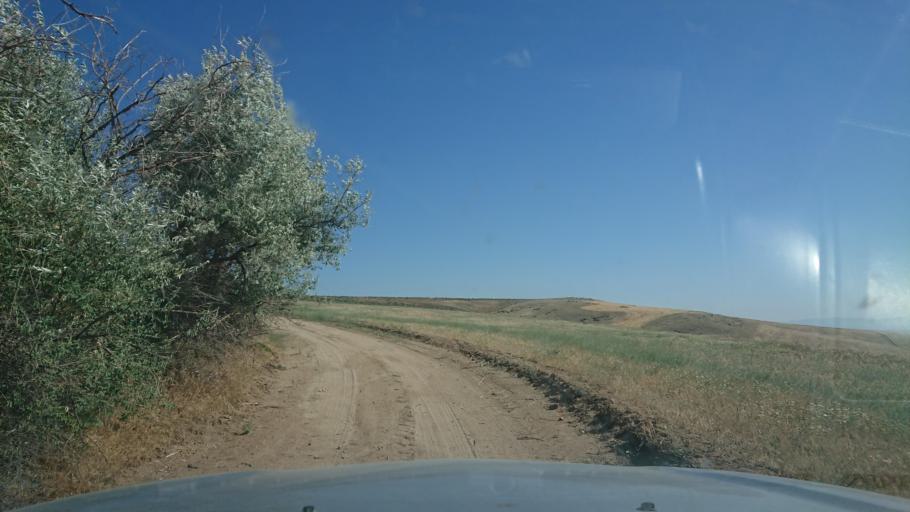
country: TR
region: Aksaray
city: Agacoren
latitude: 38.8458
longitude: 33.9183
